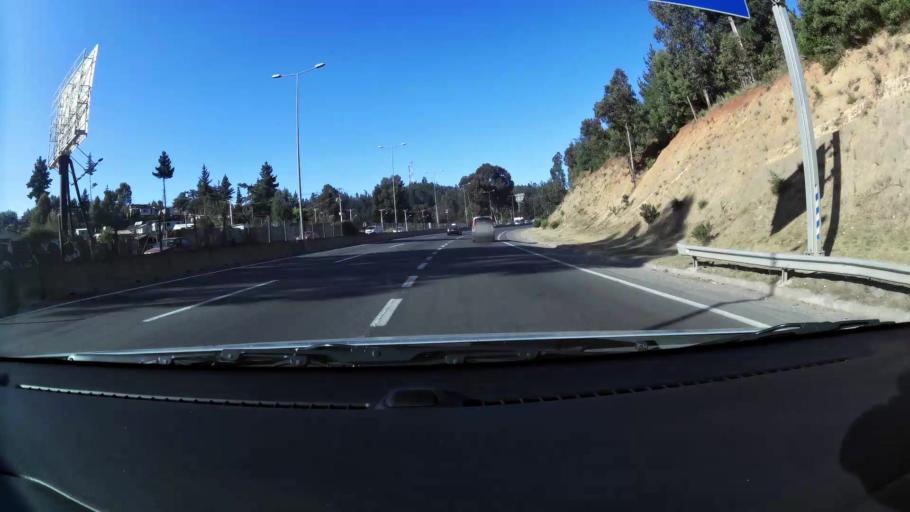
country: CL
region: Valparaiso
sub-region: Provincia de Valparaiso
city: Vina del Mar
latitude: -33.1109
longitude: -71.5595
